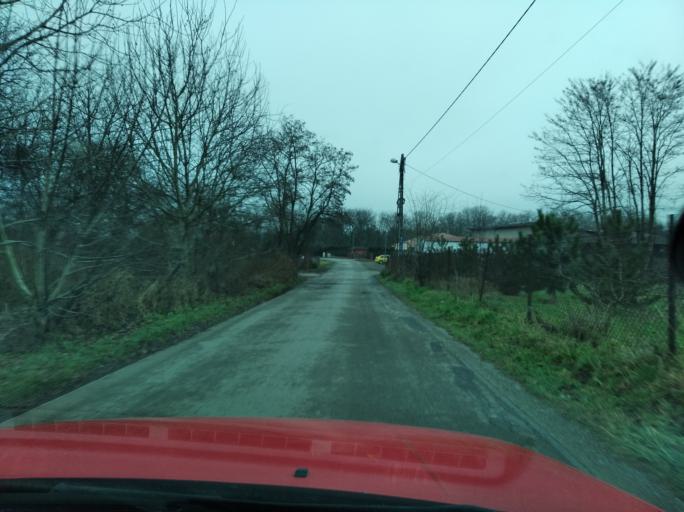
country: PL
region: Subcarpathian Voivodeship
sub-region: Powiat jaroslawski
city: Pawlosiow
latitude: 50.0155
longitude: 22.6330
